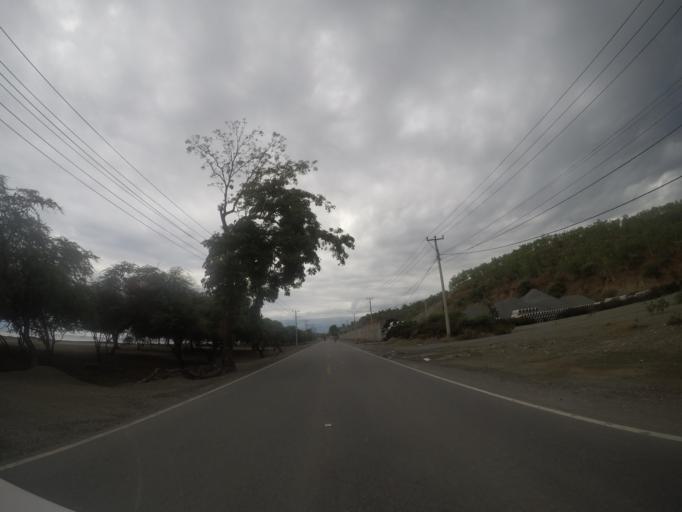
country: TL
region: Liquica
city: Liquica
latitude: -8.5647
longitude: 125.4016
